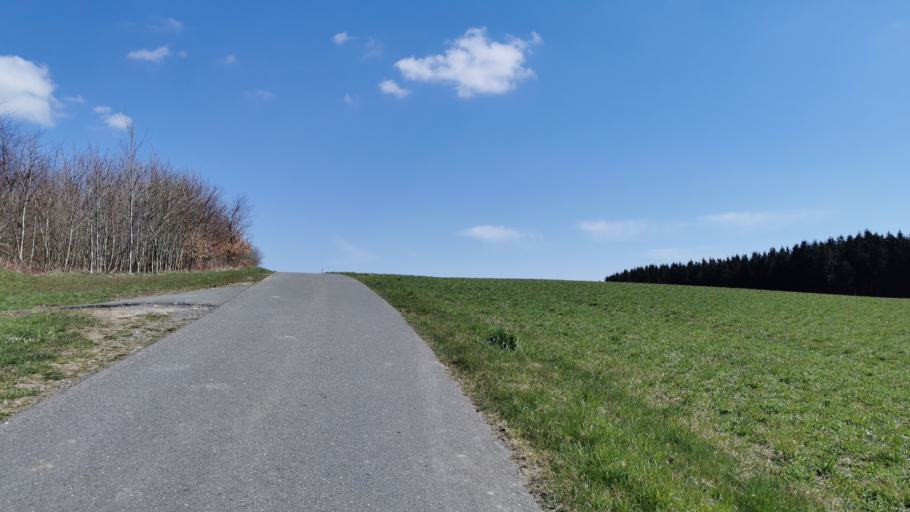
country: DE
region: Bavaria
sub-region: Upper Franconia
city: Teuschnitz
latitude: 50.4094
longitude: 11.3918
